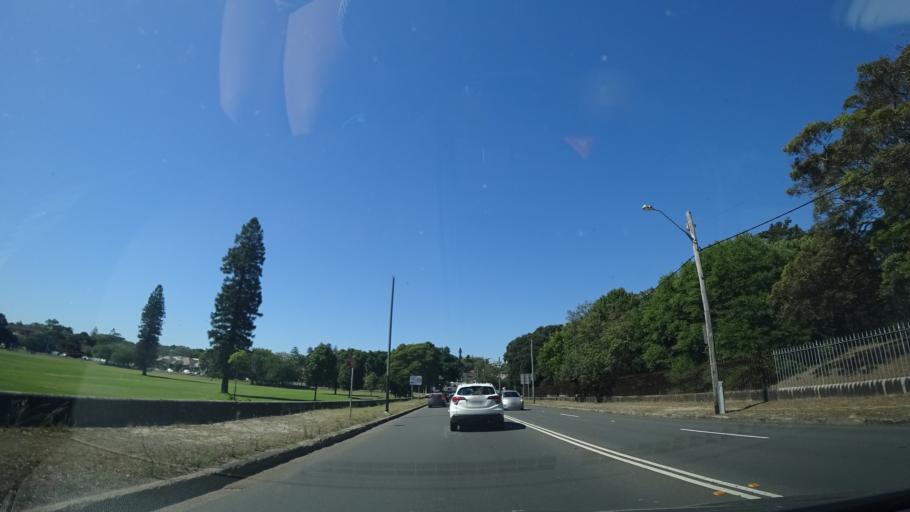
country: AU
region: New South Wales
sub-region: Waverley
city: Bondi Junction
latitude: -33.9015
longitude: 151.2451
